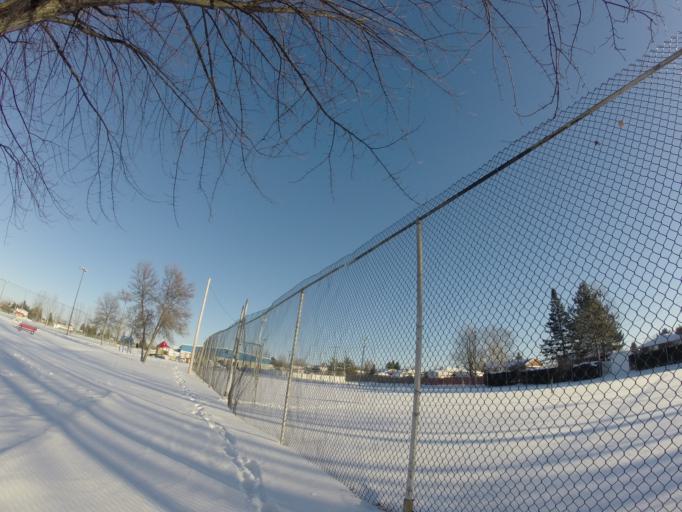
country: CA
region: Ontario
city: Rayside-Balfour
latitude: 46.5749
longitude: -81.1949
